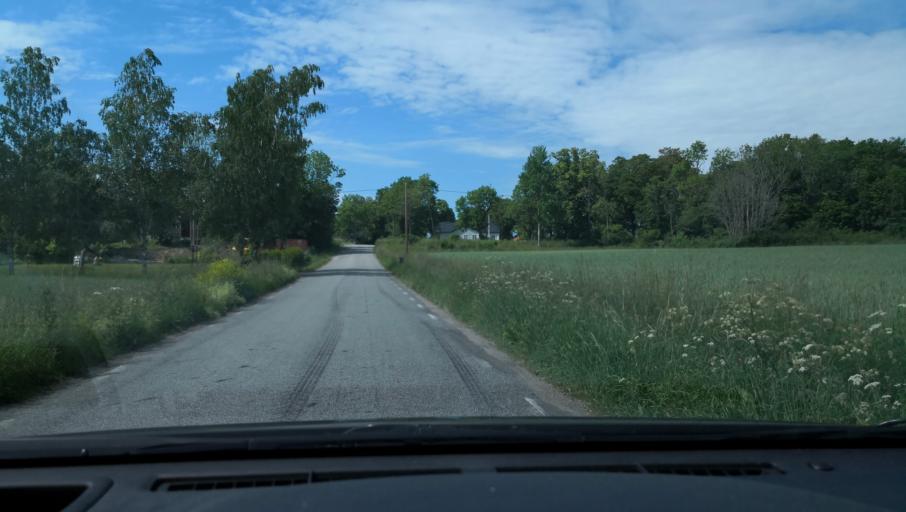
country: SE
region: Stockholm
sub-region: Sigtuna Kommun
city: Sigtuna
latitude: 59.6781
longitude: 17.6969
